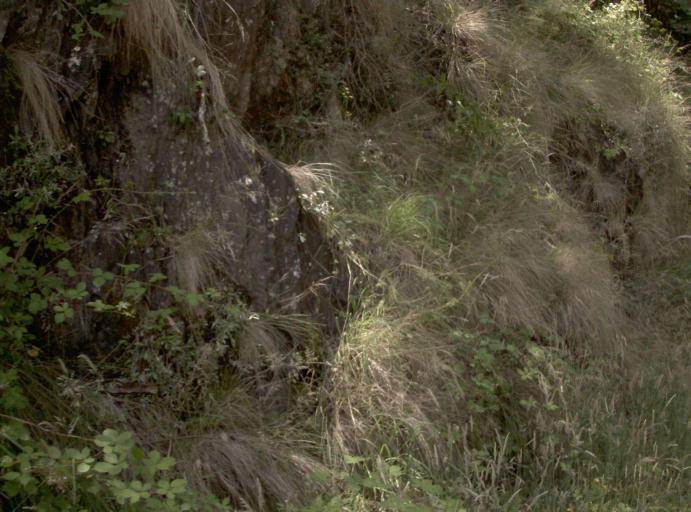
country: AU
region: Victoria
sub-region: Latrobe
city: Traralgon
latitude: -37.9519
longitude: 146.4463
